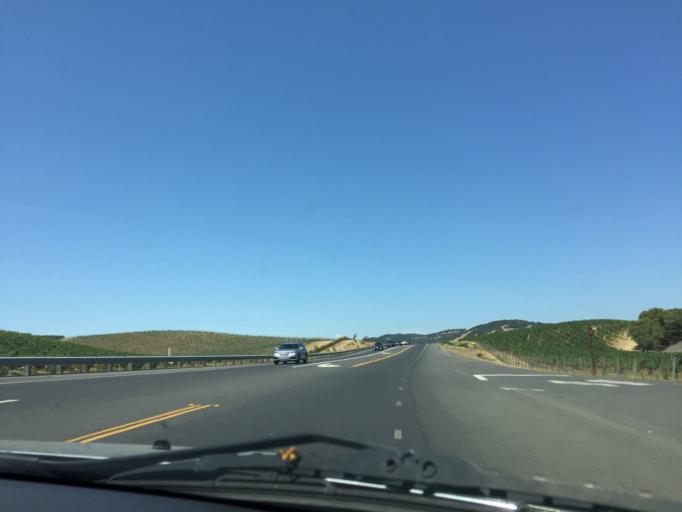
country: US
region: California
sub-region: Napa County
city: Napa
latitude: 38.2566
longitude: -122.3513
